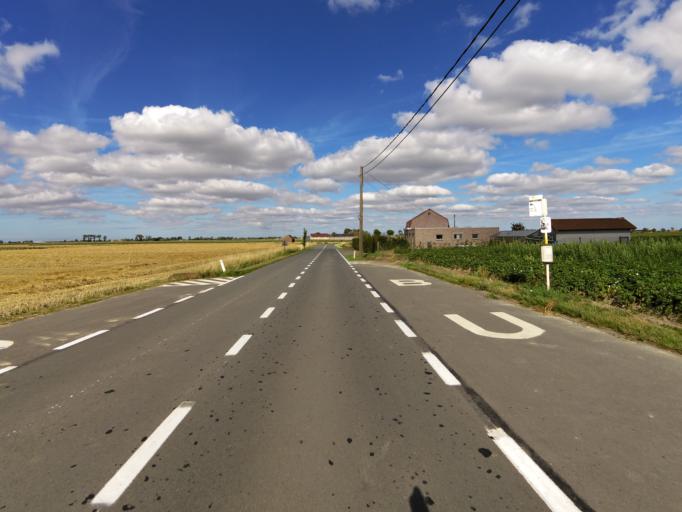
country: FR
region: Nord-Pas-de-Calais
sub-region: Departement du Nord
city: Hondschoote
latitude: 50.9493
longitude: 2.6411
